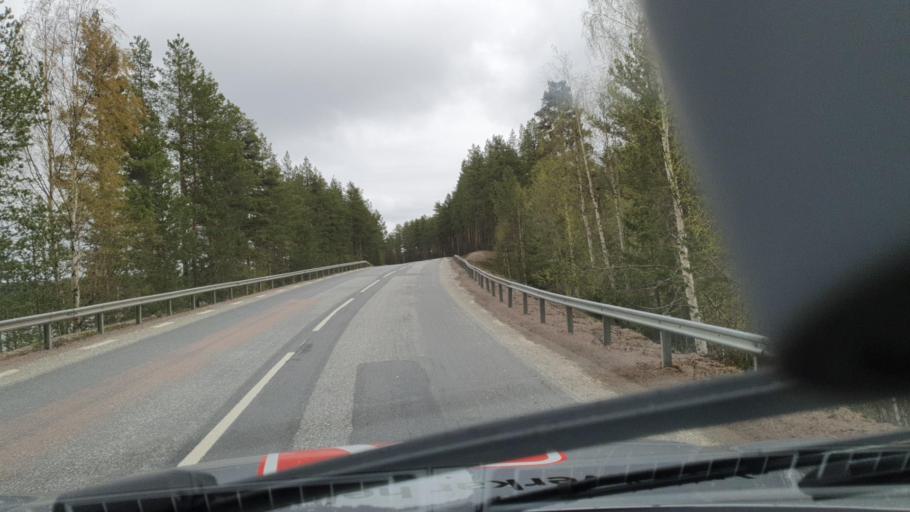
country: SE
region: Vaesternorrland
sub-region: Solleftea Kommun
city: Solleftea
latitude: 63.6477
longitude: 17.3793
